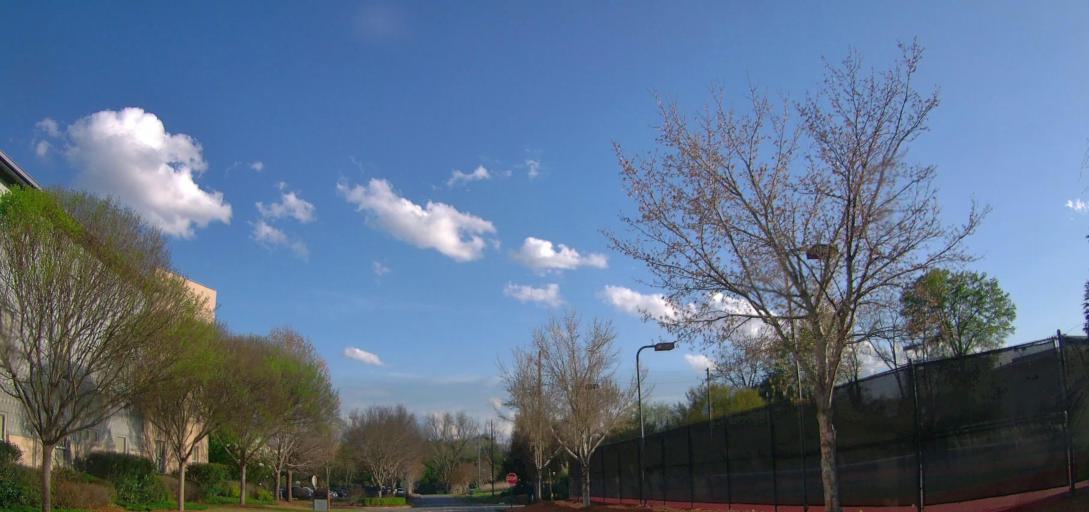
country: US
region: Georgia
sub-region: Baldwin County
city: Milledgeville
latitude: 33.0798
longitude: -83.2214
